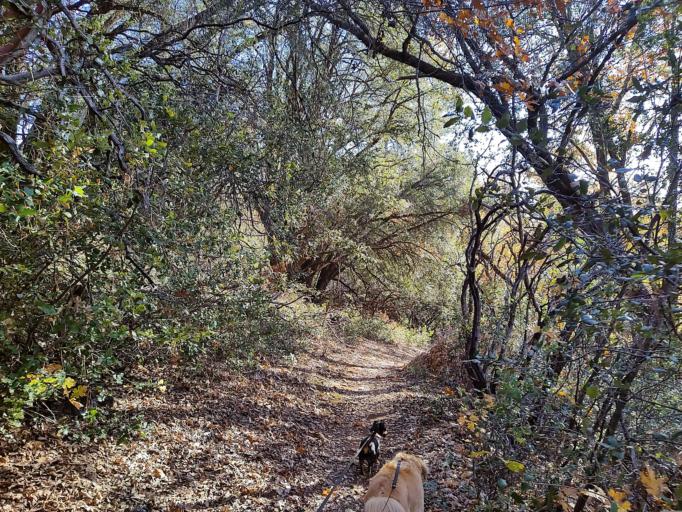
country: US
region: California
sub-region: Placer County
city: Meadow Vista
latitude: 39.0225
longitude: -120.9845
